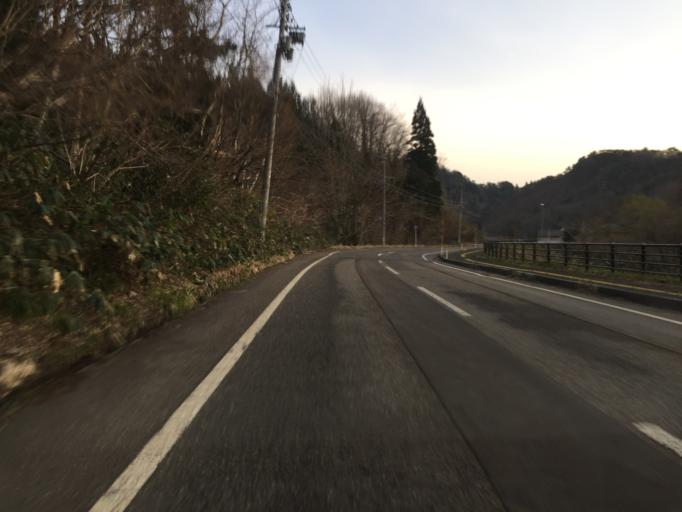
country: JP
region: Niigata
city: Suibara
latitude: 37.7138
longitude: 139.3696
